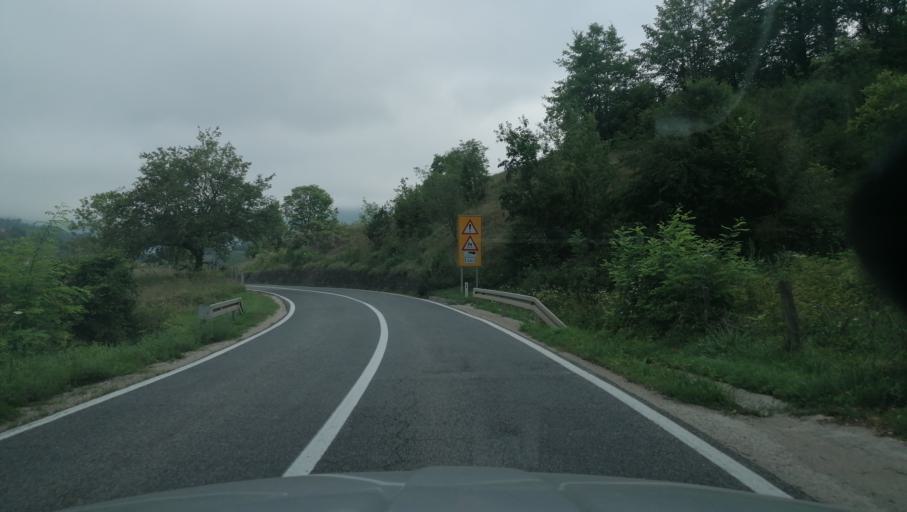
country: BA
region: Federation of Bosnia and Herzegovina
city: Divicani
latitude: 44.3558
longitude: 17.3001
